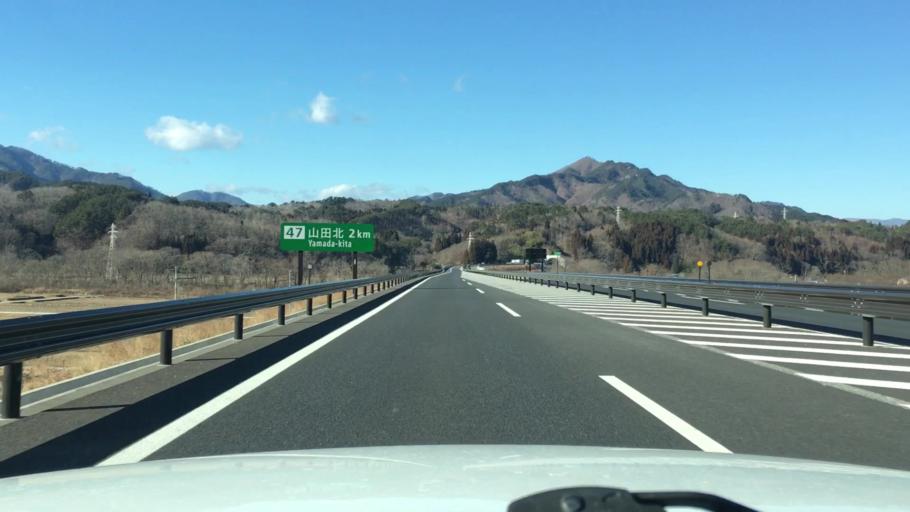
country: JP
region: Iwate
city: Yamada
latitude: 39.5236
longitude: 141.9284
